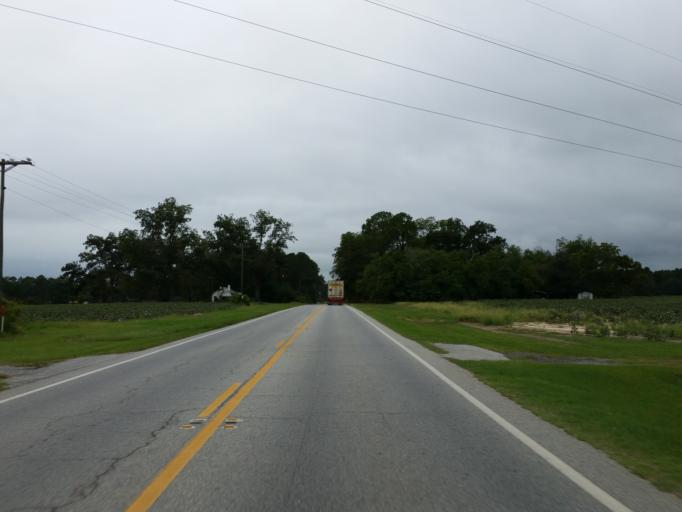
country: US
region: Georgia
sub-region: Cook County
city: Adel
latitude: 31.1382
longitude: -83.4044
